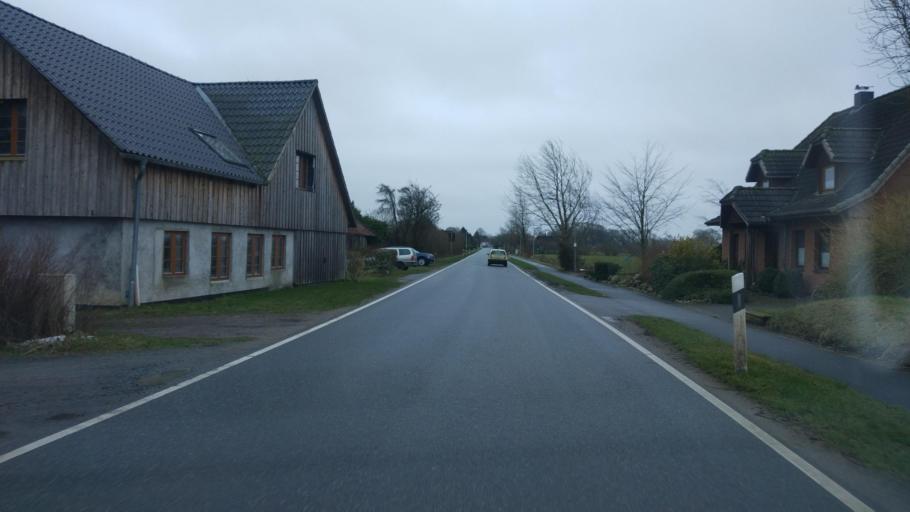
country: DE
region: Schleswig-Holstein
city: Ellingstedt
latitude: 54.4826
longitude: 9.4095
